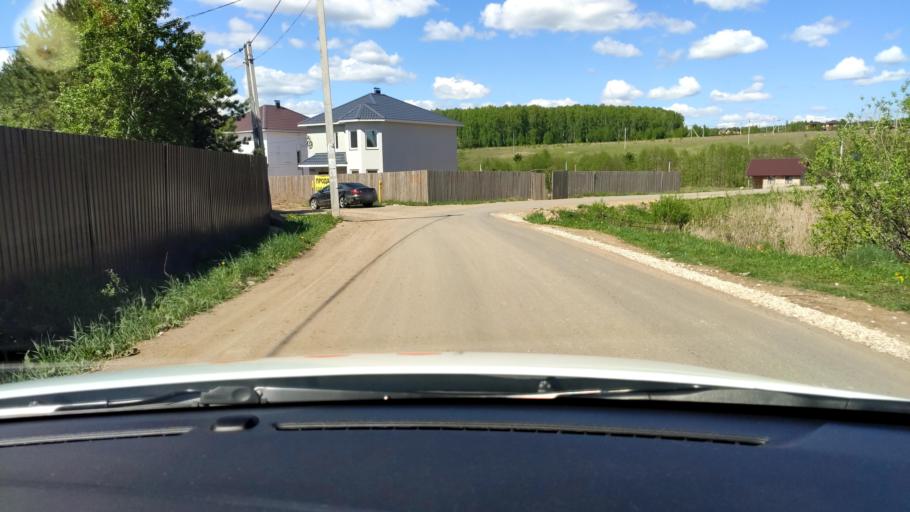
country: RU
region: Tatarstan
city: Vysokaya Gora
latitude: 55.8184
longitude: 49.2819
